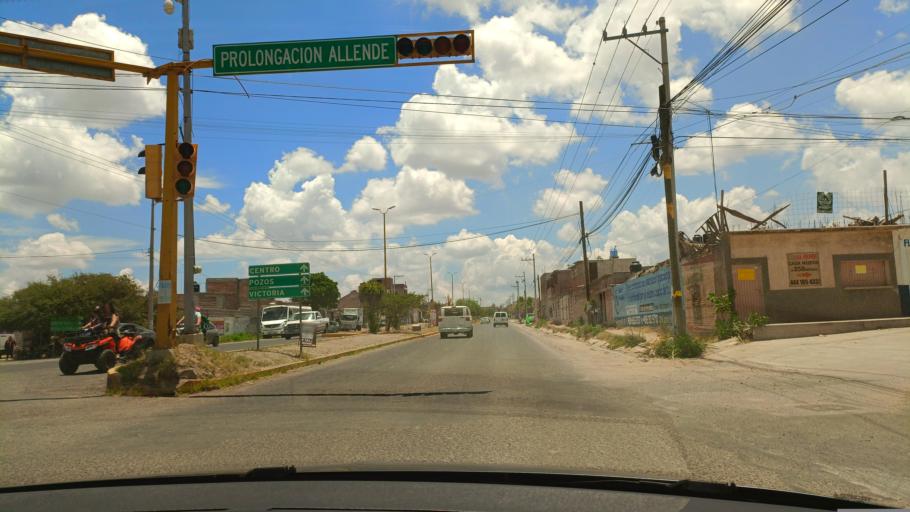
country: MX
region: Guanajuato
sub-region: San Luis de la Paz
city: San Ignacio
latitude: 21.2875
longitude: -100.5307
